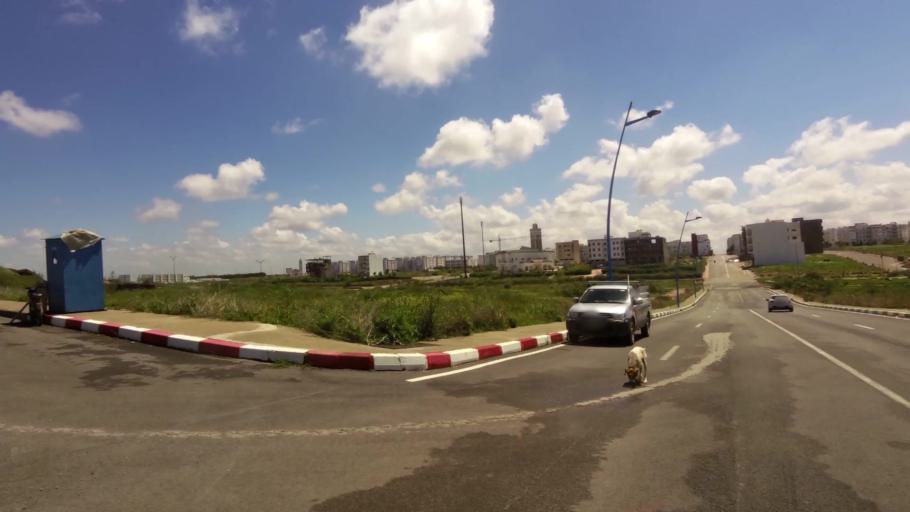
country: MA
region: Grand Casablanca
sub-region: Nouaceur
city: Dar Bouazza
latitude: 33.5212
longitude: -7.7778
